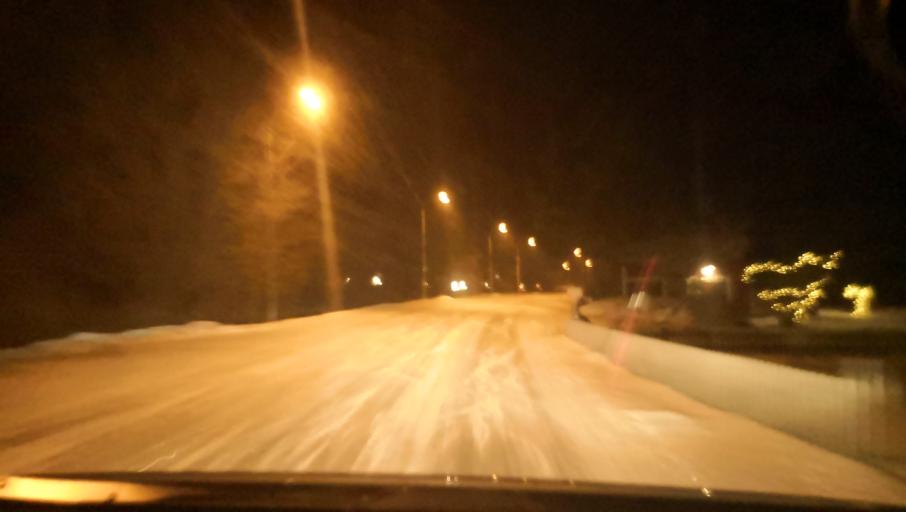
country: SE
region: Uppsala
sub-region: Heby Kommun
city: Tarnsjo
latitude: 60.1452
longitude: 16.9136
